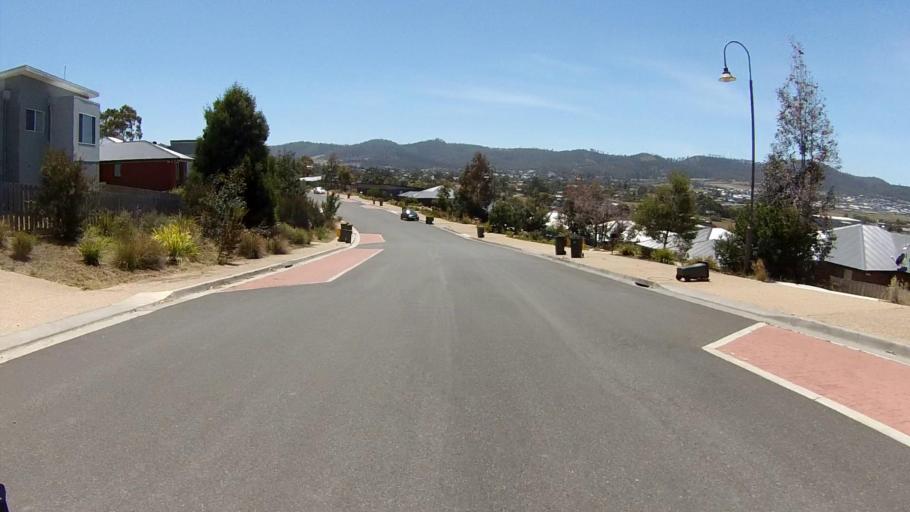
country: AU
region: Tasmania
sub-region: Clarence
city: Rokeby
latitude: -42.9082
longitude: 147.4285
